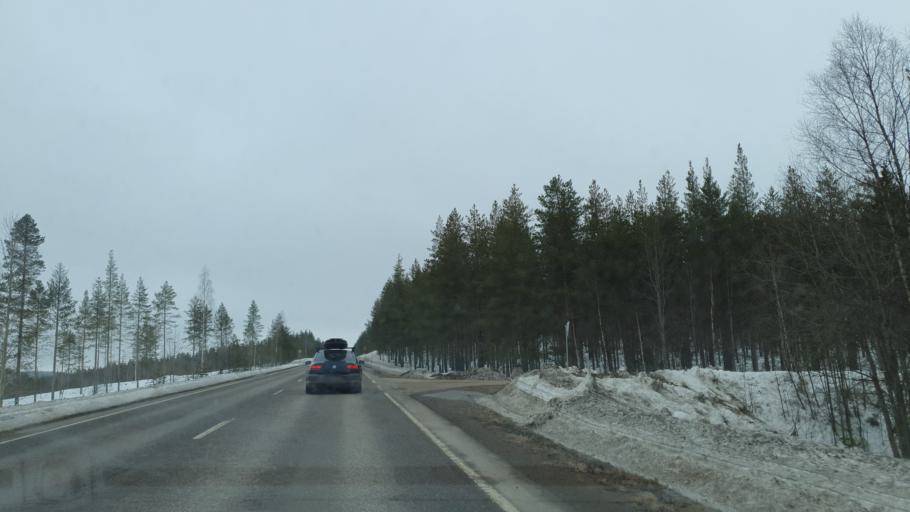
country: FI
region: Lapland
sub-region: Torniolaakso
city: Pello
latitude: 66.8546
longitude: 24.0456
